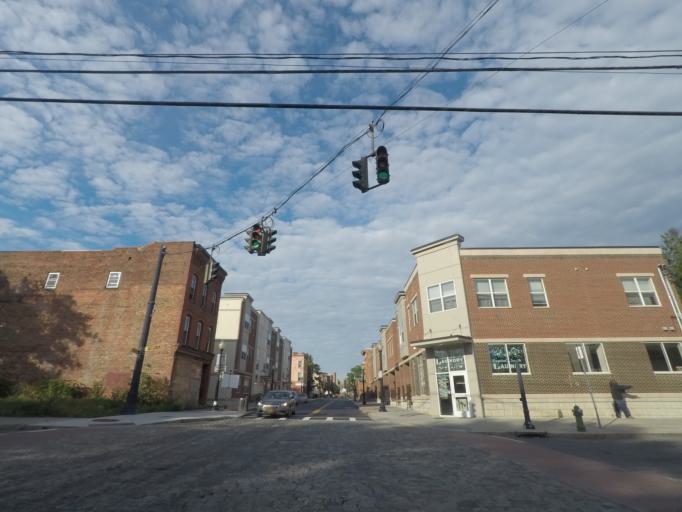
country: US
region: New York
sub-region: Albany County
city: Albany
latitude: 42.6390
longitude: -73.7583
